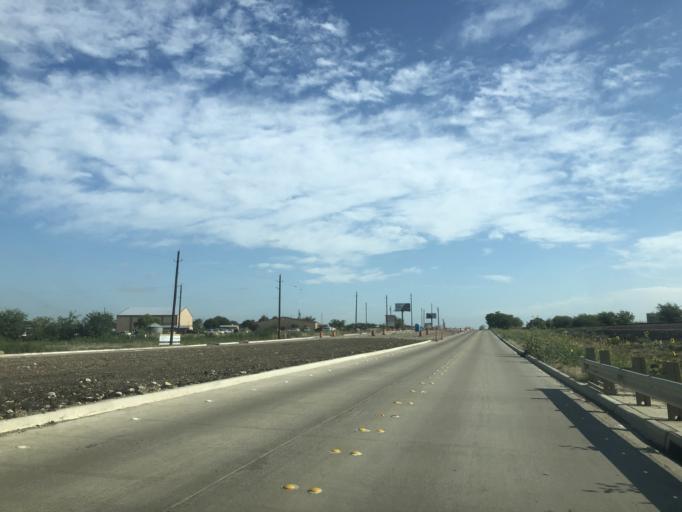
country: US
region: Texas
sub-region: Denton County
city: Justin
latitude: 33.0604
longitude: -97.2981
